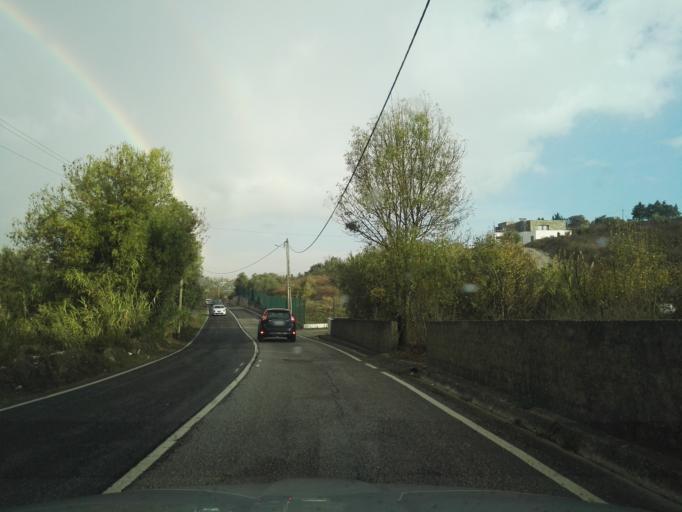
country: PT
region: Lisbon
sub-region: Arruda Dos Vinhos
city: Arruda dos Vinhos
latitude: 38.9671
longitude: -9.0641
